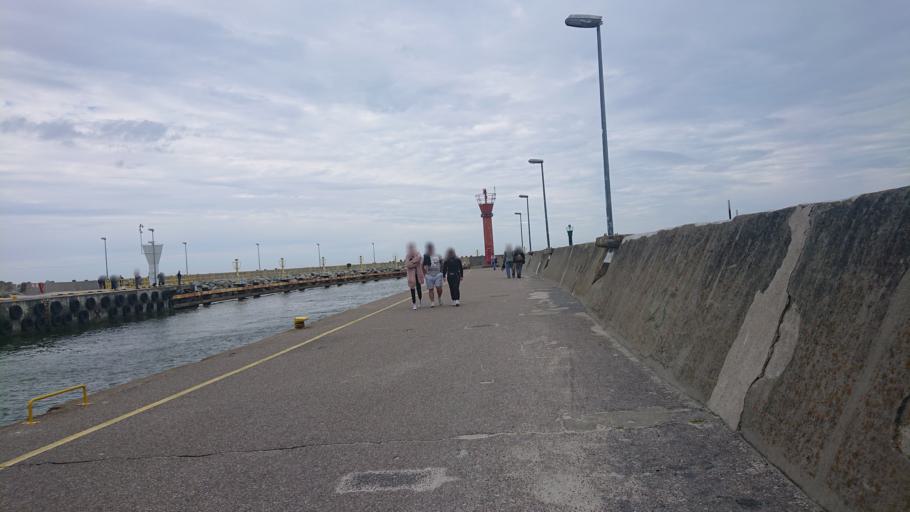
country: PL
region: Pomeranian Voivodeship
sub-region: Powiat leborski
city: Leba
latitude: 54.7684
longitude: 17.5512
